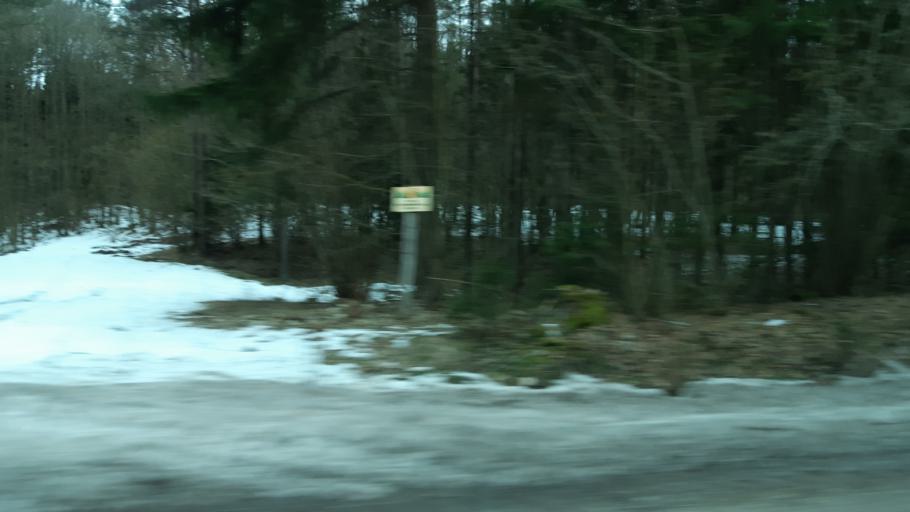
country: PL
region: Podlasie
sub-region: Suwalki
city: Suwalki
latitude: 54.2886
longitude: 22.9543
